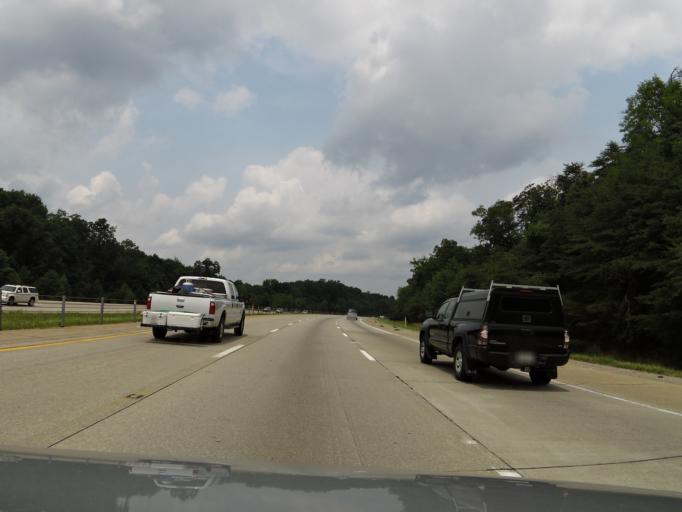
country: US
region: Kentucky
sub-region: Bullitt County
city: Shepherdsville
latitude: 37.9580
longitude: -85.6924
